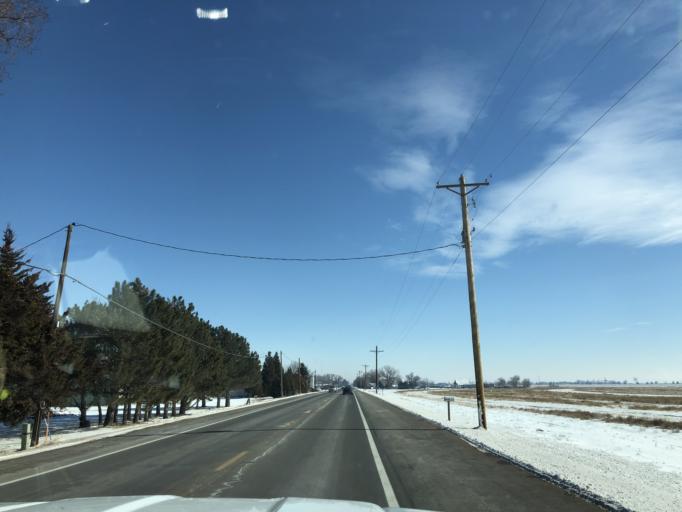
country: US
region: Colorado
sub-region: Morgan County
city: Fort Morgan
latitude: 40.2541
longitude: -103.8647
